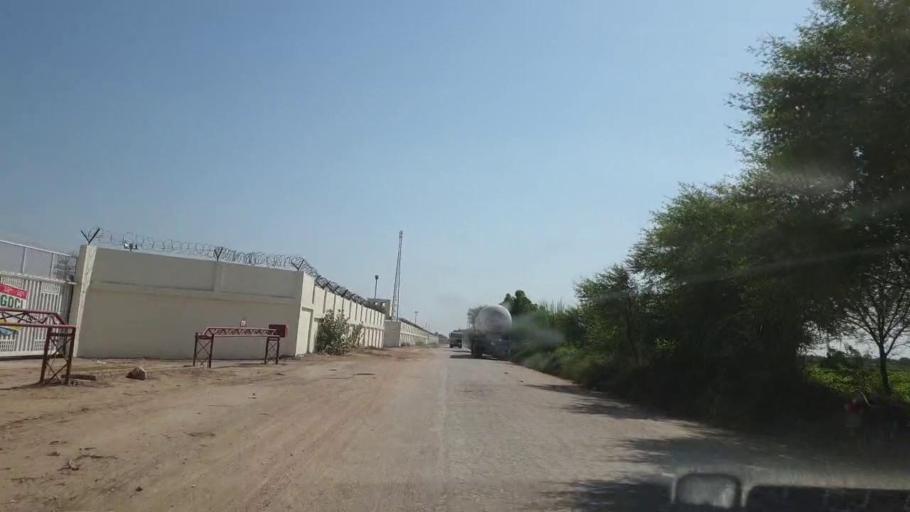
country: PK
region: Sindh
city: Tando Jam
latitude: 25.3875
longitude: 68.5791
